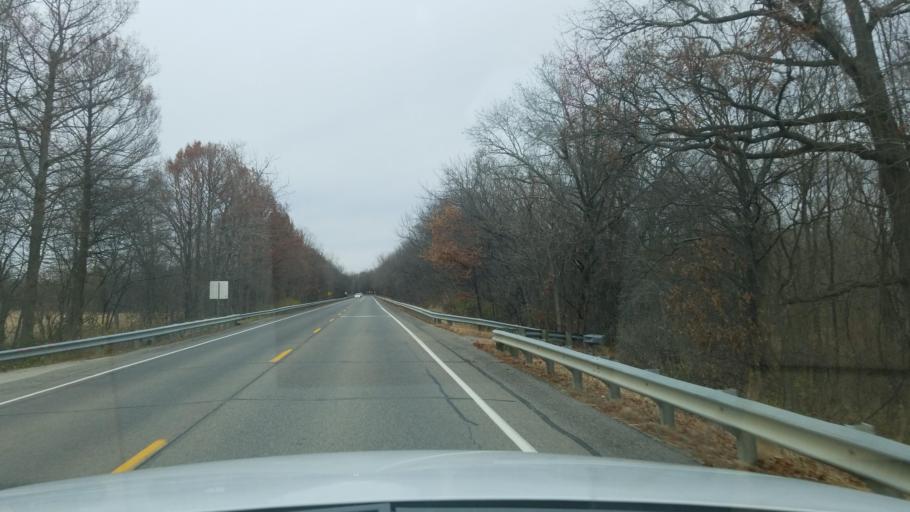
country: US
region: Indiana
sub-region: Posey County
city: Mount Vernon
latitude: 37.9402
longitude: -88.0141
